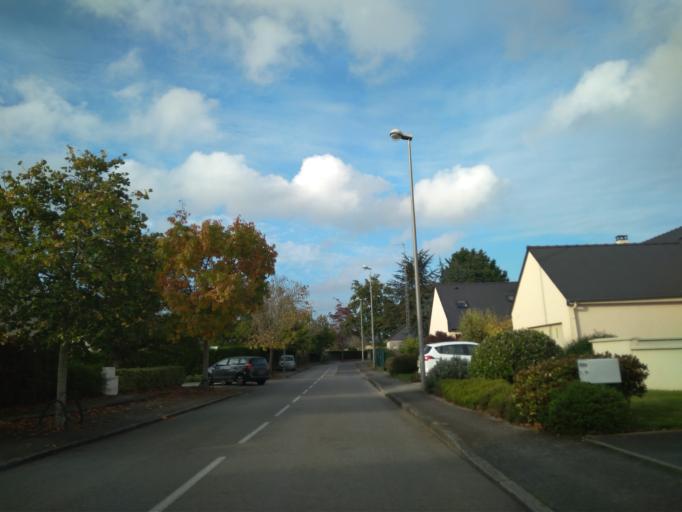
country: FR
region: Brittany
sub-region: Departement d'Ille-et-Vilaine
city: Betton
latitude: 48.1732
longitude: -1.6373
